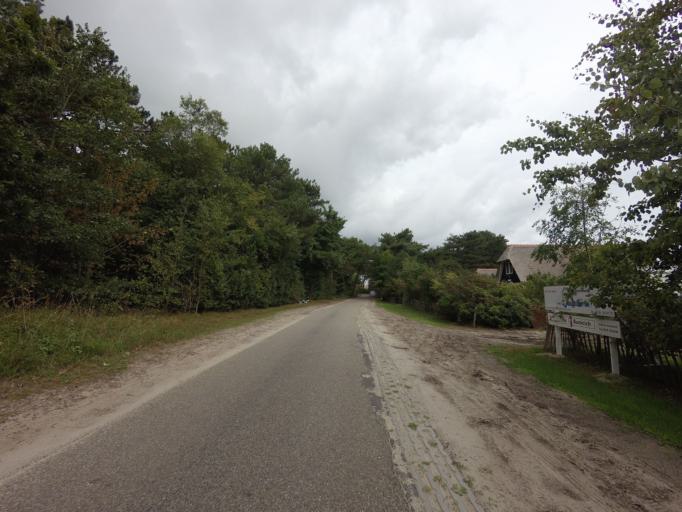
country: NL
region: Friesland
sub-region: Gemeente Ameland
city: Hollum
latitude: 53.4471
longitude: 5.6270
